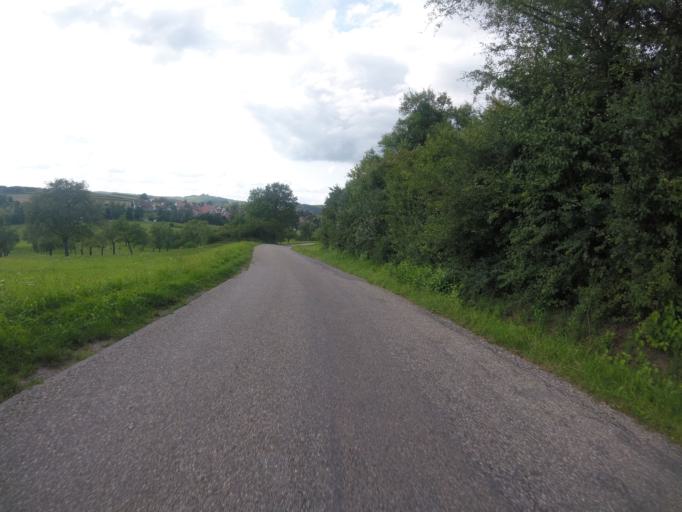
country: DE
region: Baden-Wuerttemberg
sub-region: Regierungsbezirk Stuttgart
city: Aspach
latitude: 48.9832
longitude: 9.4130
